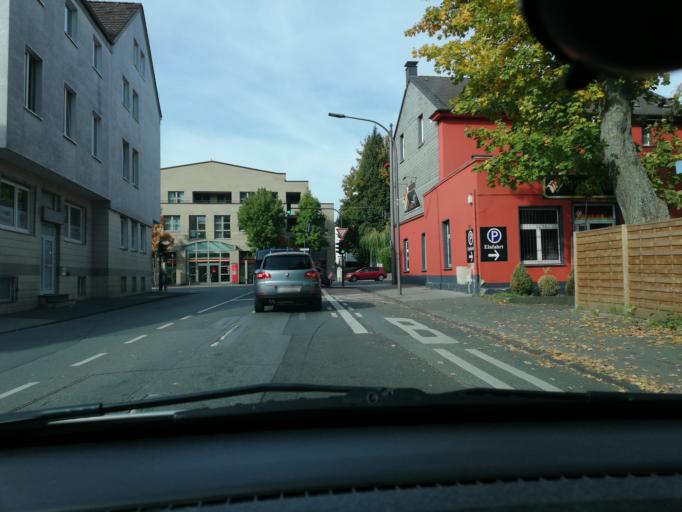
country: DE
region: North Rhine-Westphalia
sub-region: Regierungsbezirk Dusseldorf
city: Wuppertal
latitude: 51.2781
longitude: 7.1626
